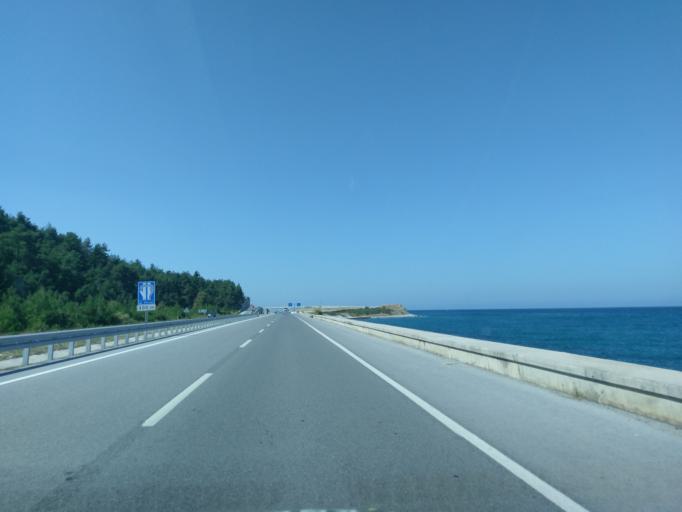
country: TR
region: Samsun
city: Yakakent
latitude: 41.6767
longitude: 35.4196
